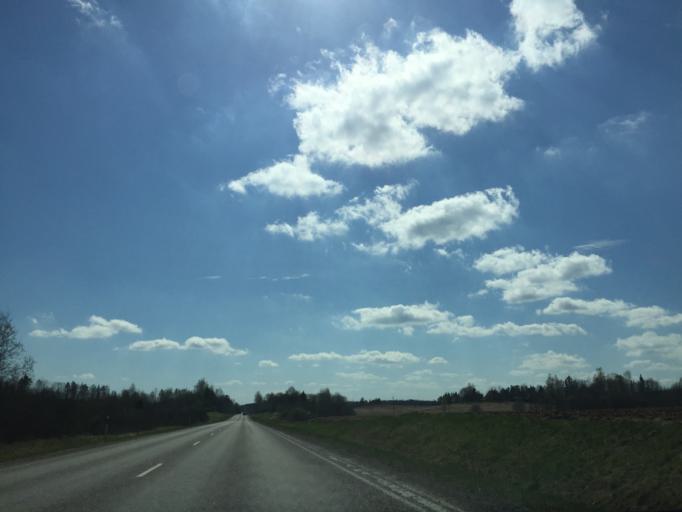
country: EE
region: Tartu
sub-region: Elva linn
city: Elva
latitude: 58.0995
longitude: 26.2312
